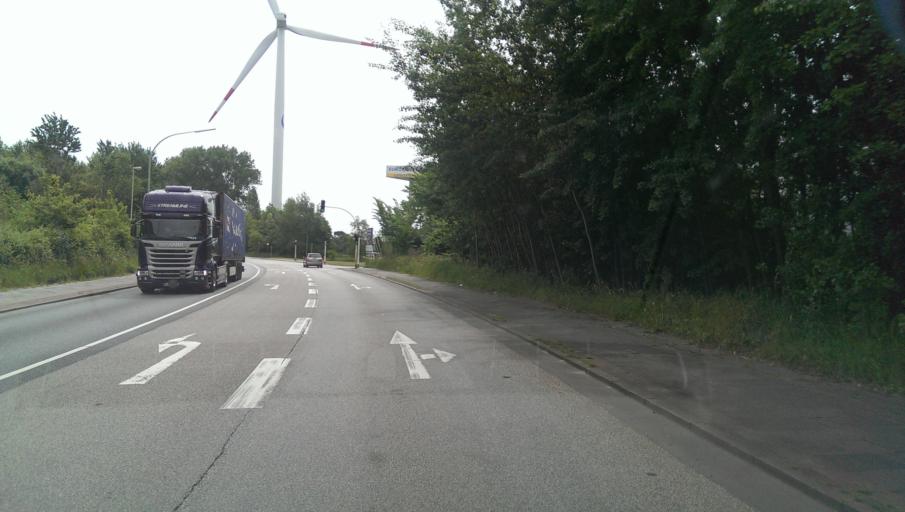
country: DE
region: Lower Saxony
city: Langen
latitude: 53.5933
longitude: 8.5463
